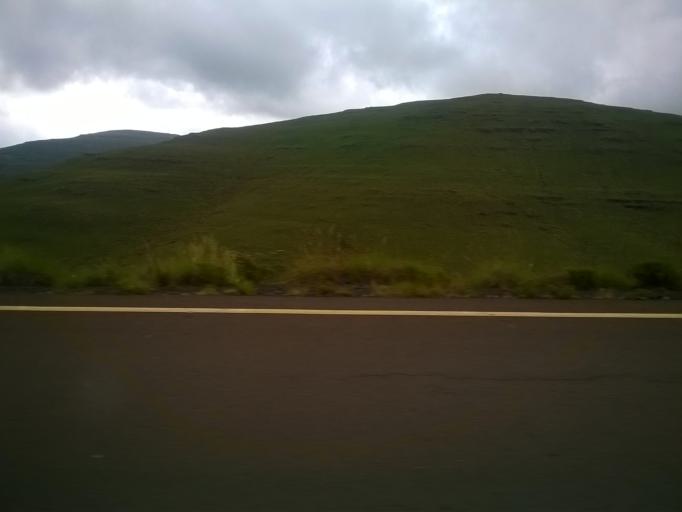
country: LS
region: Butha-Buthe
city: Butha-Buthe
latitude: -29.0896
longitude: 28.4252
